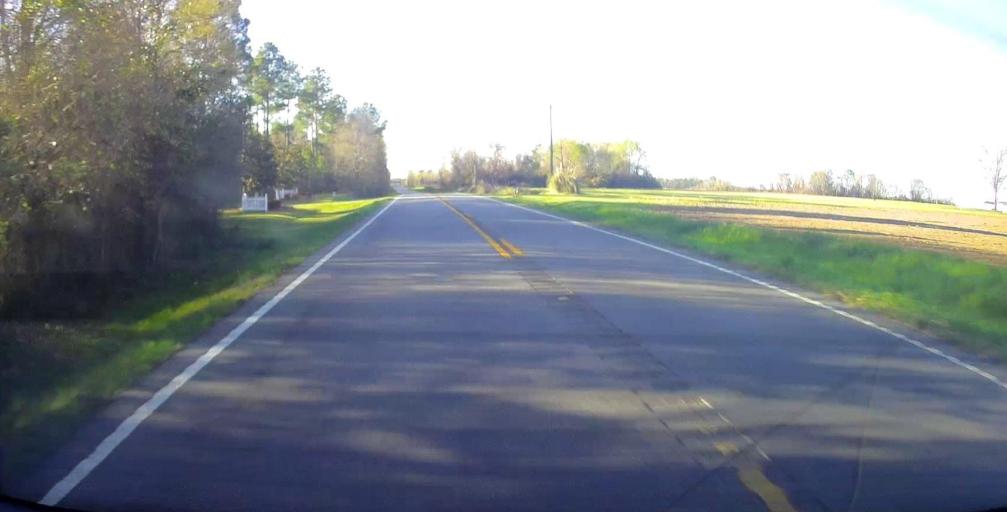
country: US
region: Georgia
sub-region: Pulaski County
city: Hawkinsville
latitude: 32.2183
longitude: -83.3862
